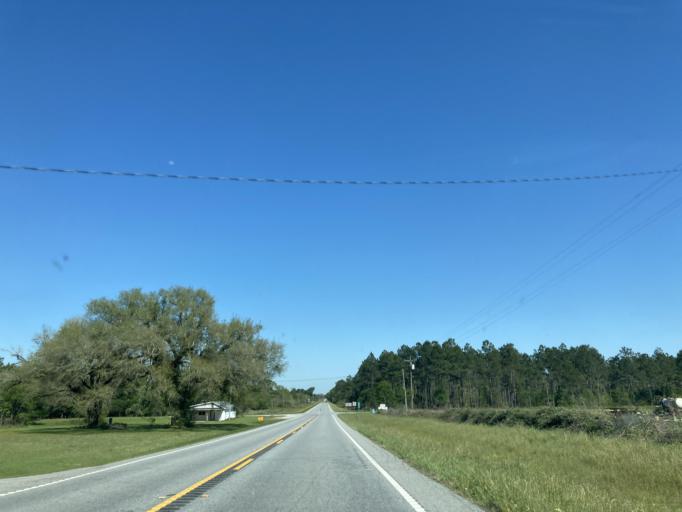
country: US
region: Georgia
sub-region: Miller County
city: Colquitt
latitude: 31.1843
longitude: -84.5718
